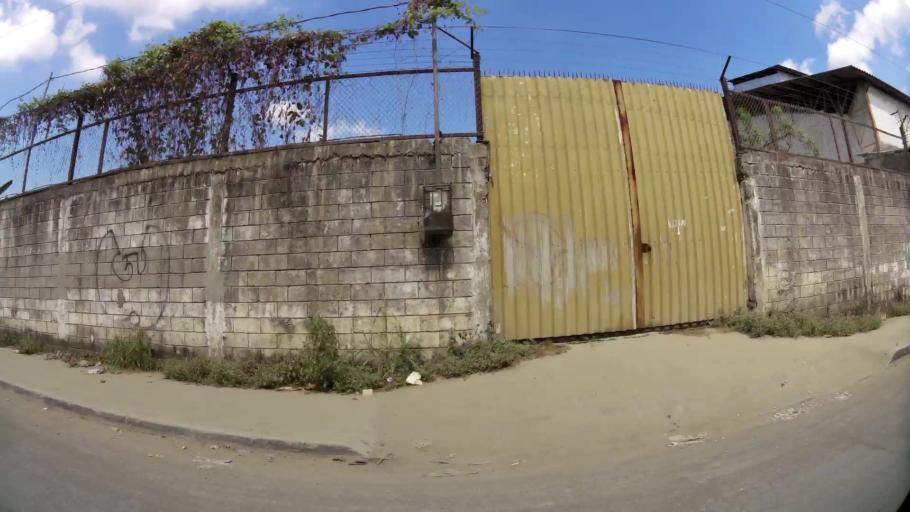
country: EC
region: Guayas
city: Guayaquil
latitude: -2.1268
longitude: -79.9301
